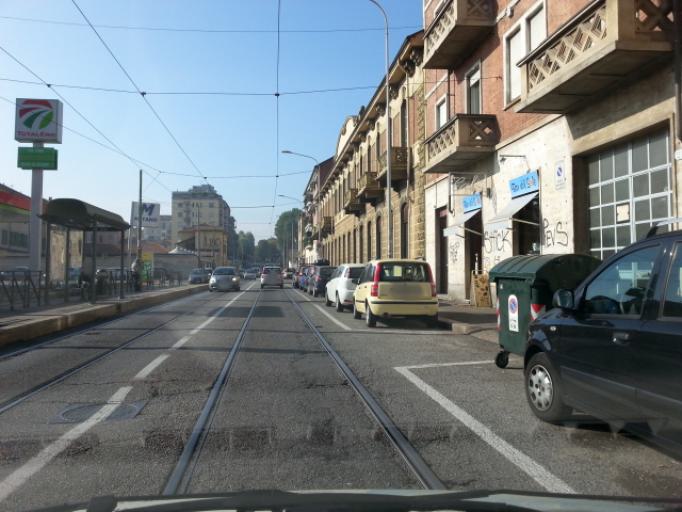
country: IT
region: Piedmont
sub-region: Provincia di Torino
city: Turin
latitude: 45.0818
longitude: 7.6781
